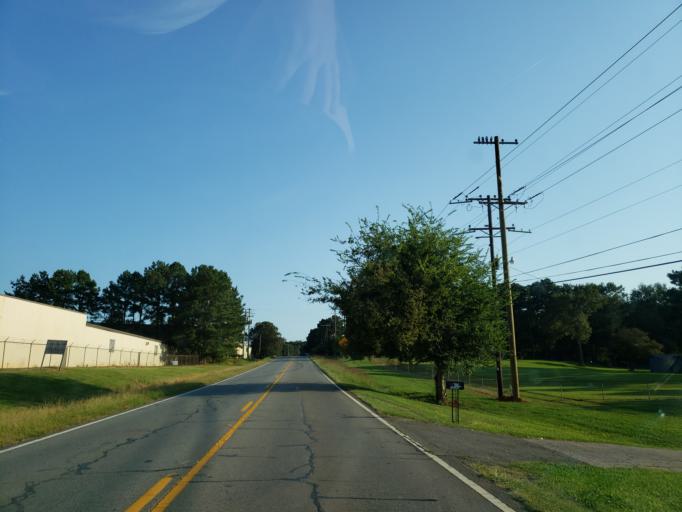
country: US
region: Georgia
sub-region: Murray County
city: Chatsworth
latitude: 34.7429
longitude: -84.8201
